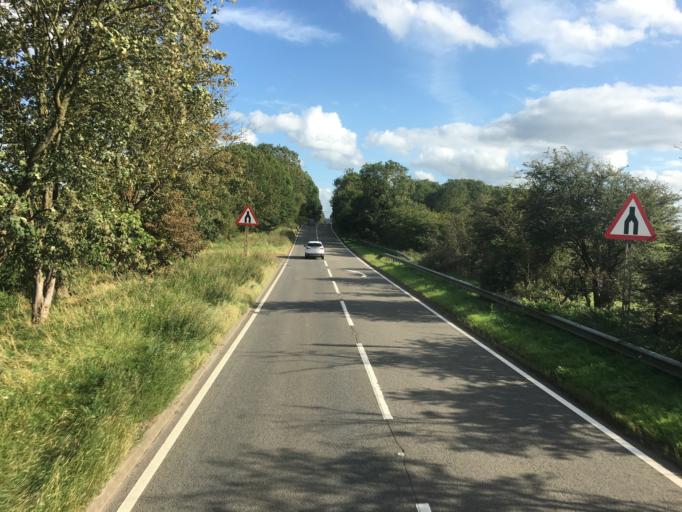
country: GB
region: England
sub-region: Leicestershire
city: Lutterworth
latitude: 52.4351
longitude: -1.2370
